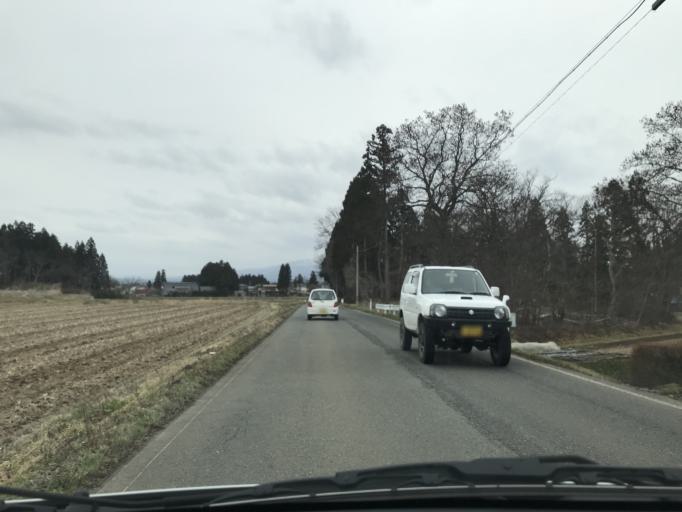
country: JP
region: Iwate
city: Kitakami
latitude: 39.3228
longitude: 141.0716
